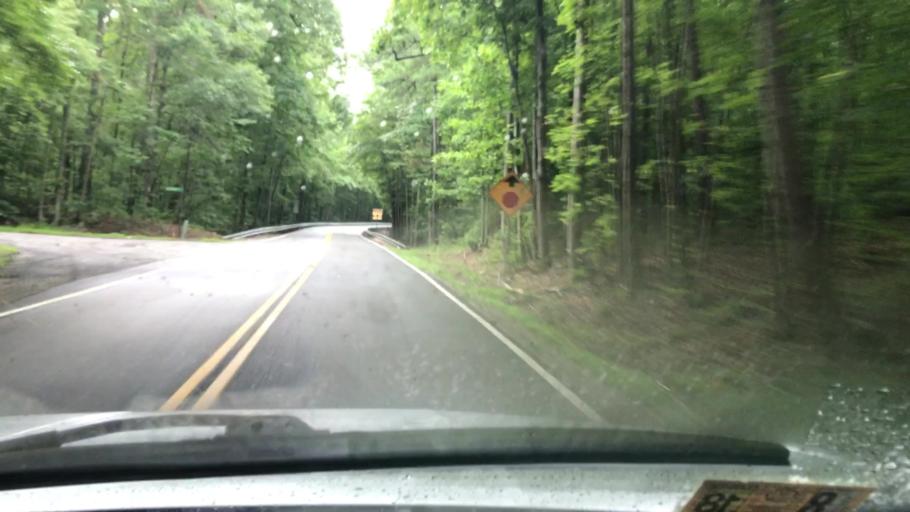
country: US
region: Virginia
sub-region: Henrico County
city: Short Pump
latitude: 37.6040
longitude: -77.6979
